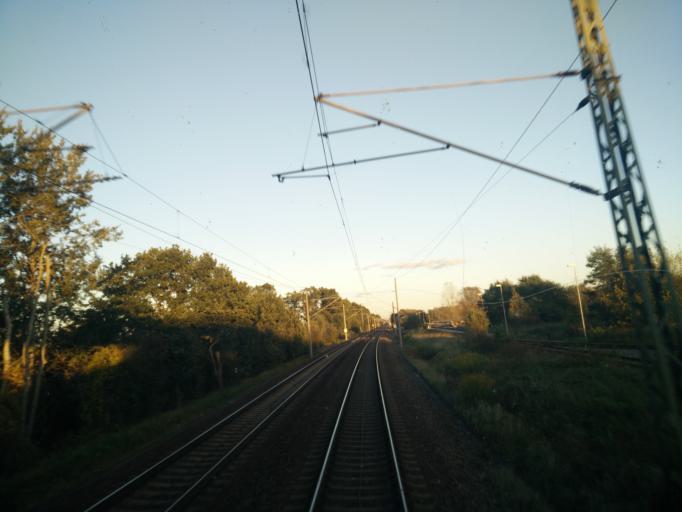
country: DE
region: Brandenburg
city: Breese
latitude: 52.9929
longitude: 11.7862
